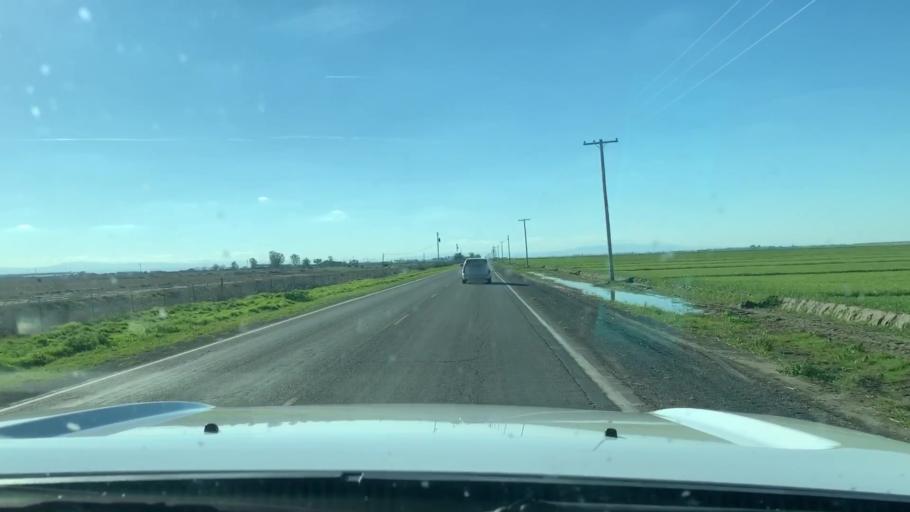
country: US
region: California
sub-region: Kings County
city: Home Garden
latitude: 36.2112
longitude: -119.6643
